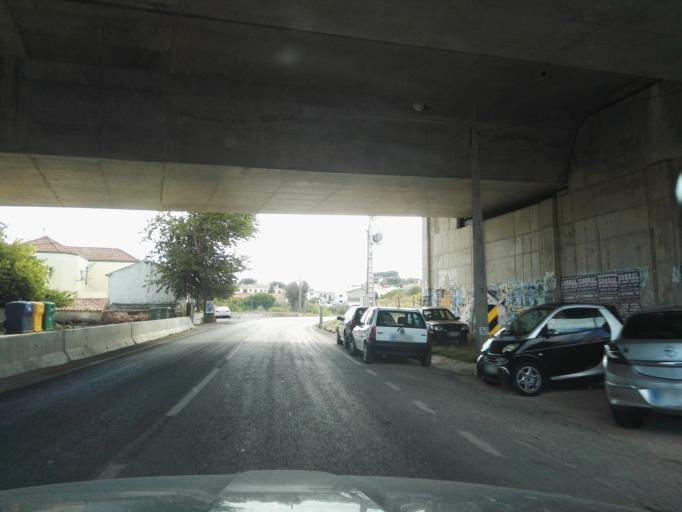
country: PT
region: Lisbon
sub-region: Arruda Dos Vinhos
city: Arruda dos Vinhos
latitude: 38.9747
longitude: -9.0596
